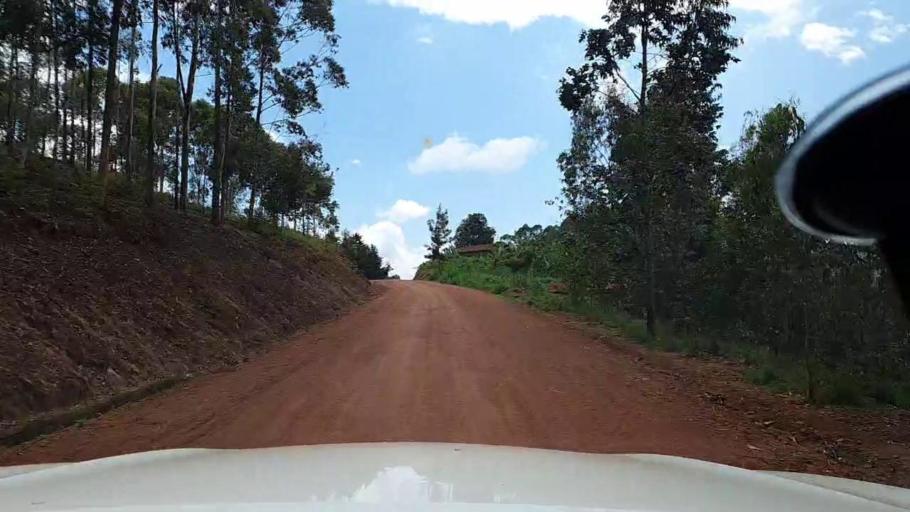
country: RW
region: Kigali
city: Kigali
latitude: -1.7657
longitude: 29.8414
